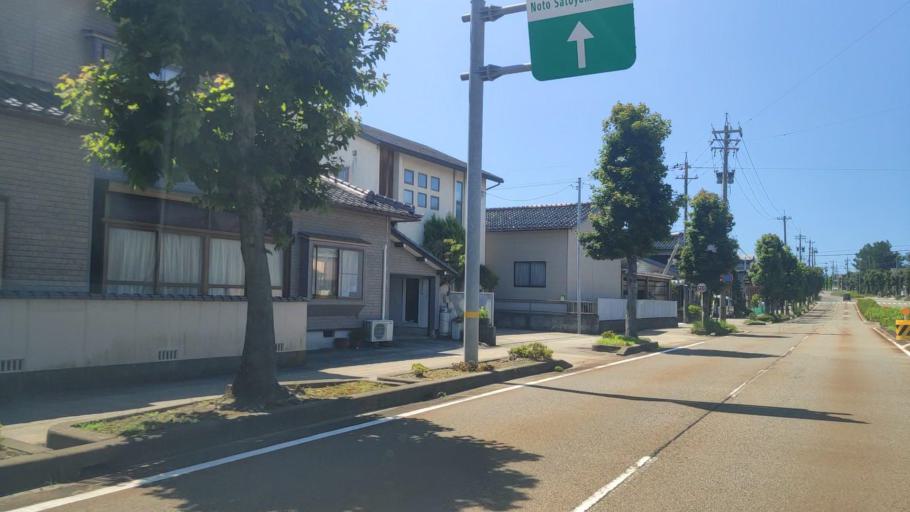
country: JP
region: Ishikawa
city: Kanazawa-shi
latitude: 36.6290
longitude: 136.6310
